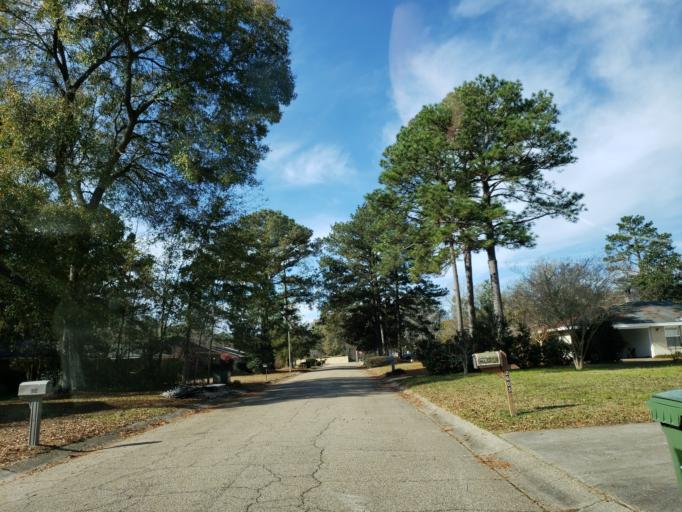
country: US
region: Mississippi
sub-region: Forrest County
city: Hattiesburg
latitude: 31.3064
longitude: -89.3274
